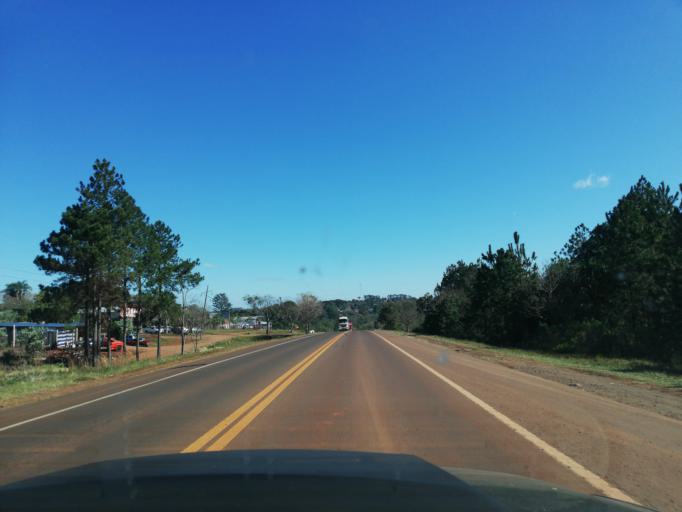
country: AR
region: Misiones
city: Aristobulo del Valle
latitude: -27.0960
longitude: -54.8719
